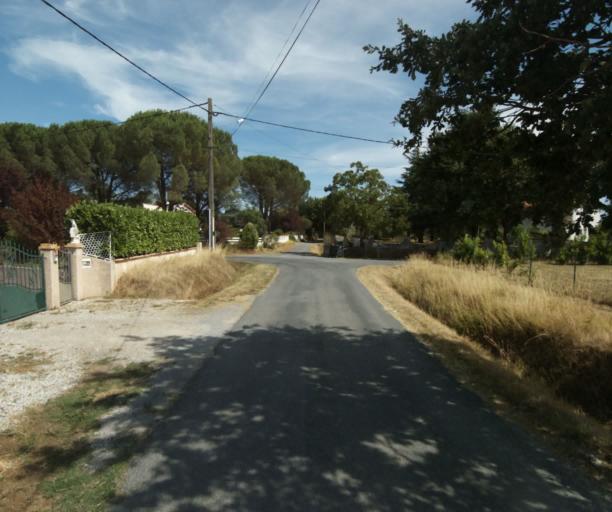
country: FR
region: Midi-Pyrenees
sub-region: Departement de la Haute-Garonne
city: Revel
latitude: 43.5114
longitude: 2.0343
